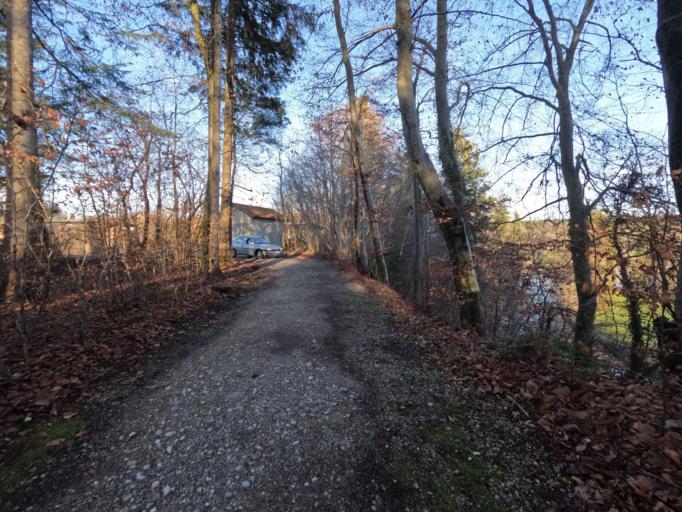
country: DE
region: Bavaria
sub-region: Upper Bavaria
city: Nussdorf
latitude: 47.9002
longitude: 12.6255
